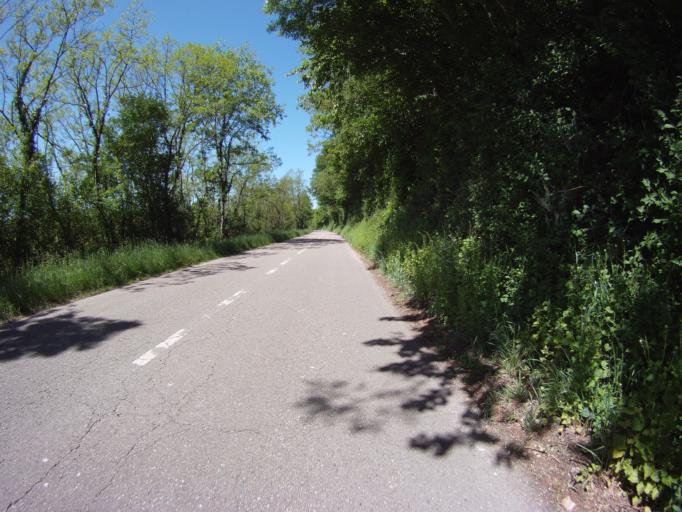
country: FR
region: Lorraine
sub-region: Departement de Meurthe-et-Moselle
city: Dommartin-les-Toul
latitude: 48.6468
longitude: 5.9310
